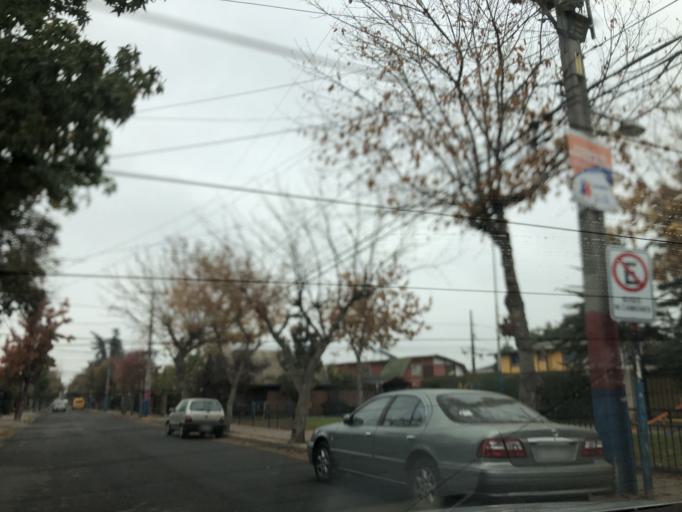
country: CL
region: Santiago Metropolitan
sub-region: Provincia de Cordillera
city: Puente Alto
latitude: -33.5905
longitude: -70.5831
